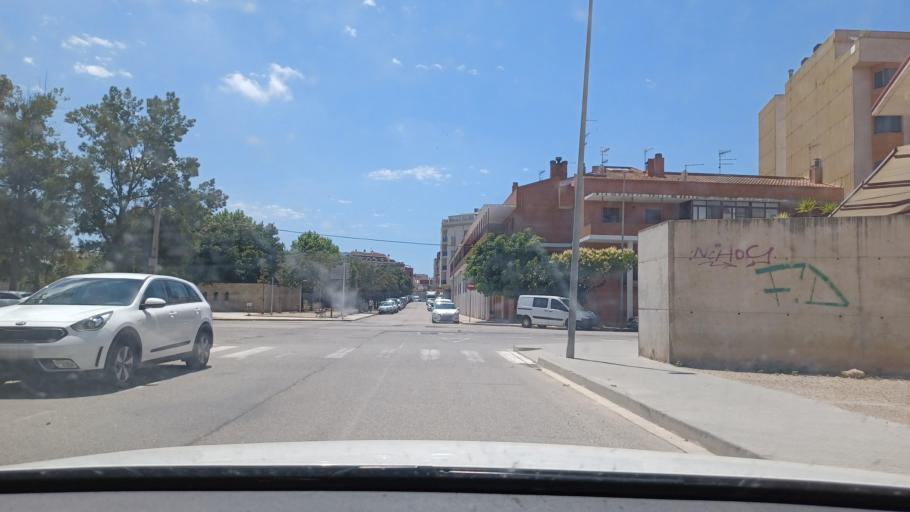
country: ES
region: Catalonia
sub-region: Provincia de Tarragona
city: Amposta
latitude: 40.7063
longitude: 0.5818
